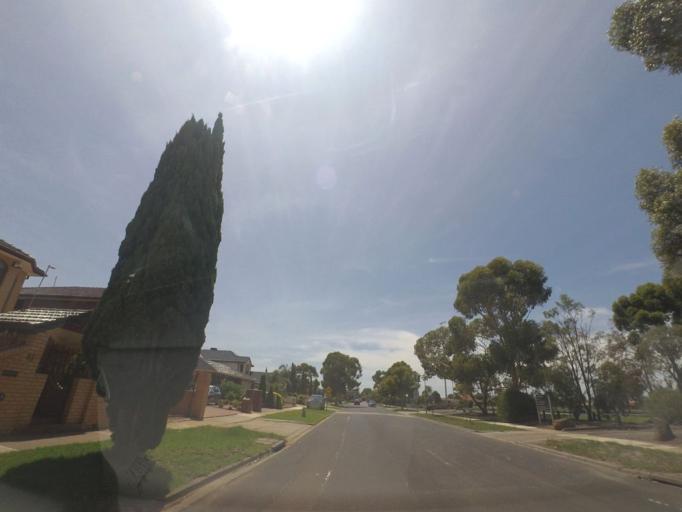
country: AU
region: Victoria
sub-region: Brimbank
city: Taylors Lakes
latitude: -37.7089
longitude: 144.7910
